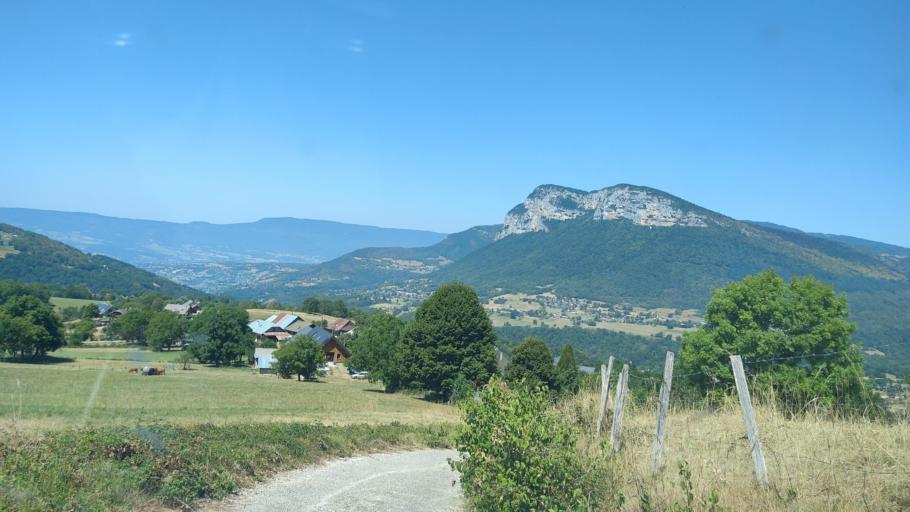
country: FR
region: Rhone-Alpes
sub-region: Departement de la Savoie
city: Barby
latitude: 45.5732
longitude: 6.0389
